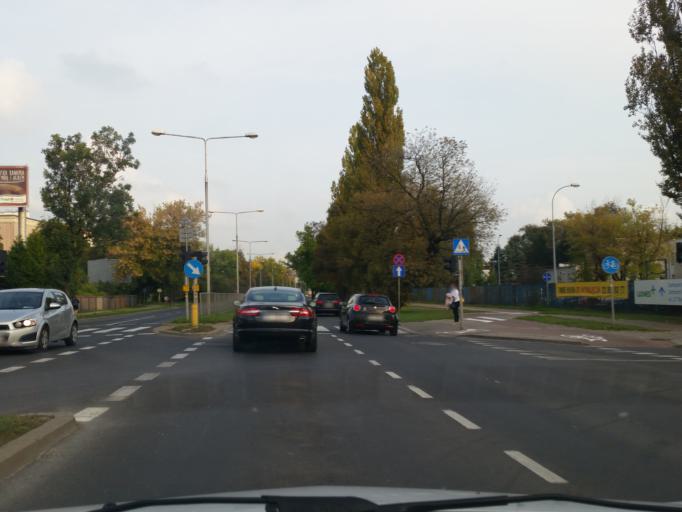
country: PL
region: Masovian Voivodeship
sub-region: Warszawa
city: Wlochy
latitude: 52.1831
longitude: 20.9699
